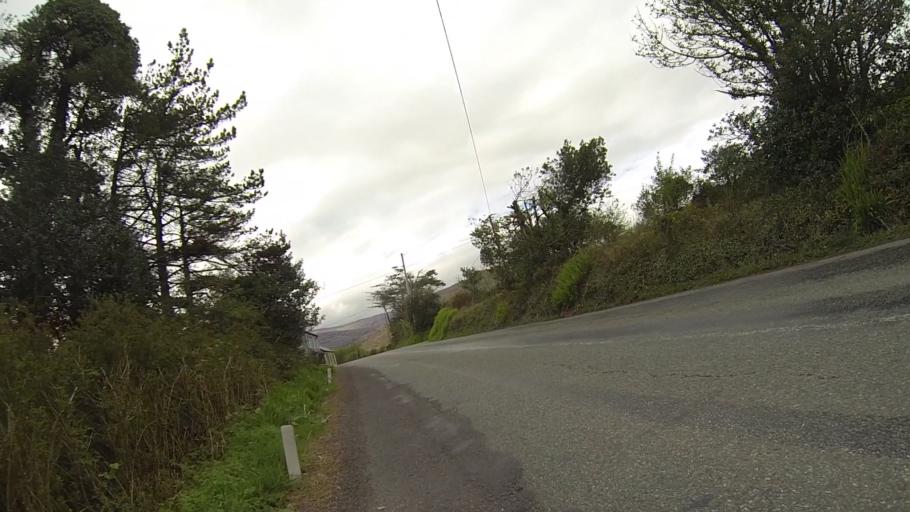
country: IE
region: Munster
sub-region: Ciarrai
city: Kenmare
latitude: 51.6860
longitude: -9.7129
